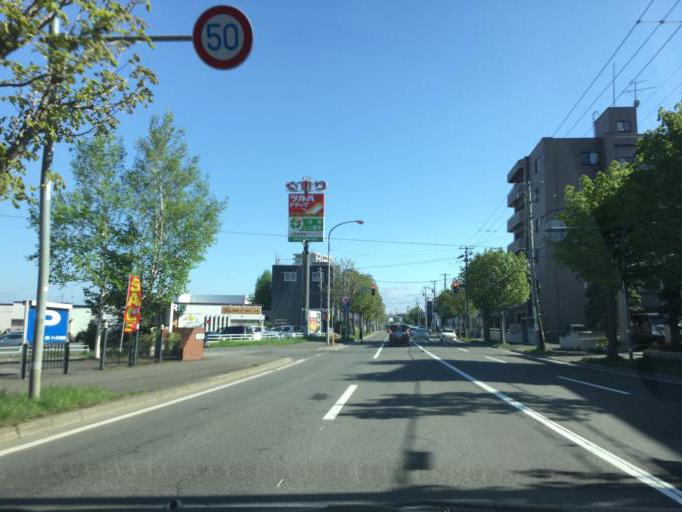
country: JP
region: Hokkaido
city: Sapporo
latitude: 43.0234
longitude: 141.4335
